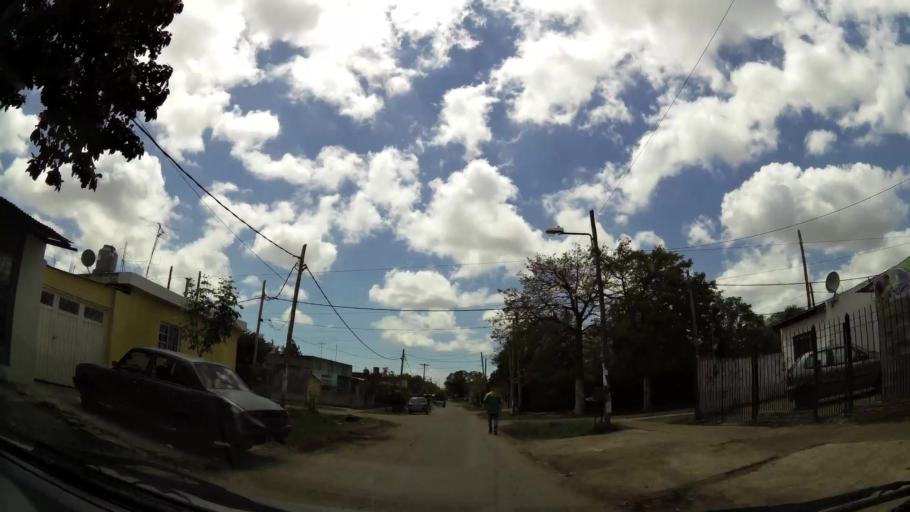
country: AR
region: Buenos Aires
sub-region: Partido de Quilmes
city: Quilmes
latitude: -34.8210
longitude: -58.2454
